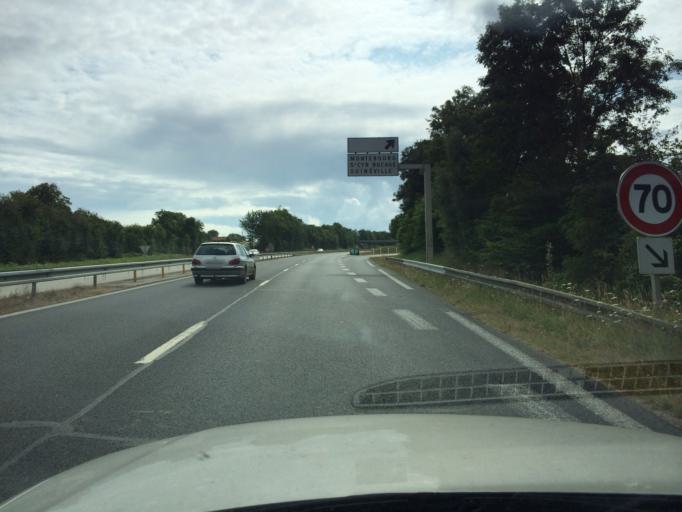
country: FR
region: Lower Normandy
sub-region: Departement de la Manche
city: Montebourg
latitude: 49.4933
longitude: -1.4114
